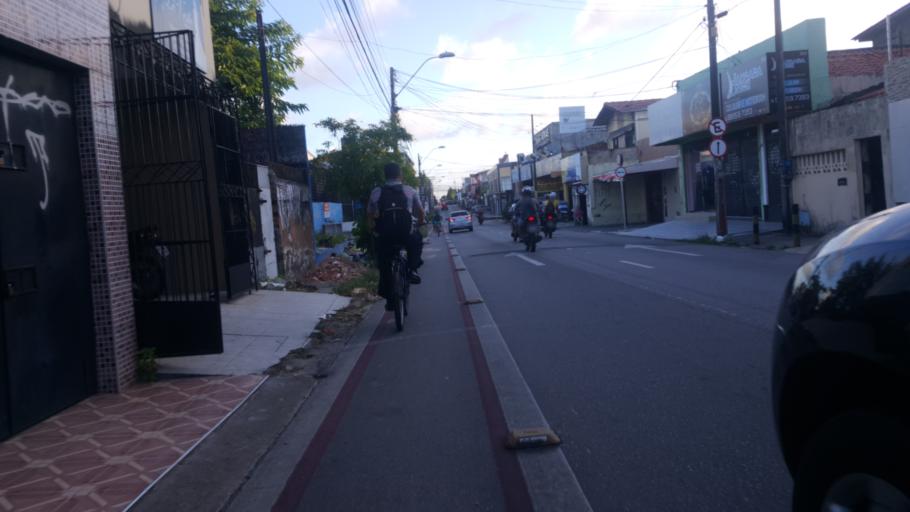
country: BR
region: Ceara
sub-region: Fortaleza
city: Fortaleza
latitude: -3.7577
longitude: -38.5437
